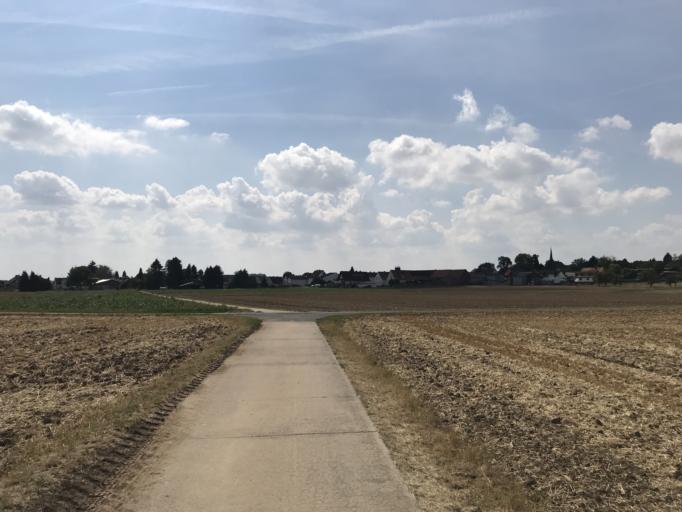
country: DE
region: Hesse
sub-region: Regierungsbezirk Darmstadt
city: Wolfersheim
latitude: 50.4443
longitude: 8.8368
